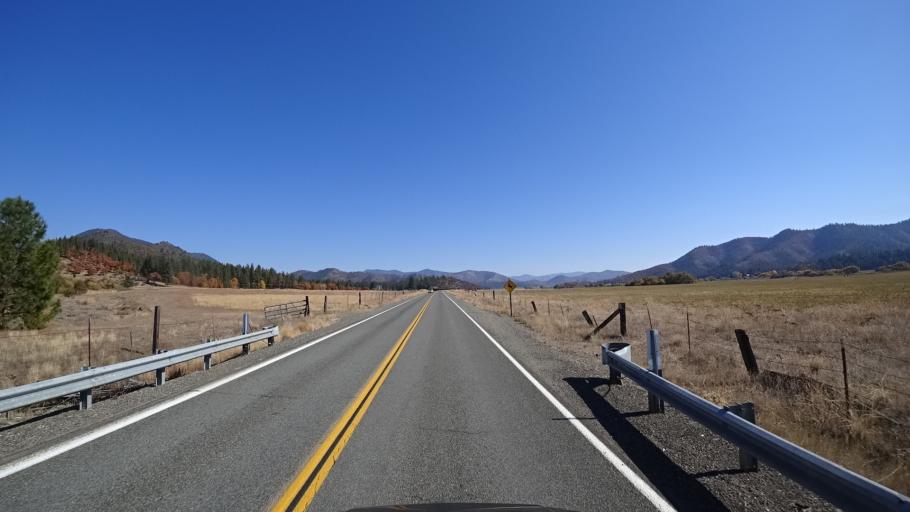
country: US
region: California
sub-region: Siskiyou County
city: Yreka
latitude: 41.6323
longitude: -122.9530
